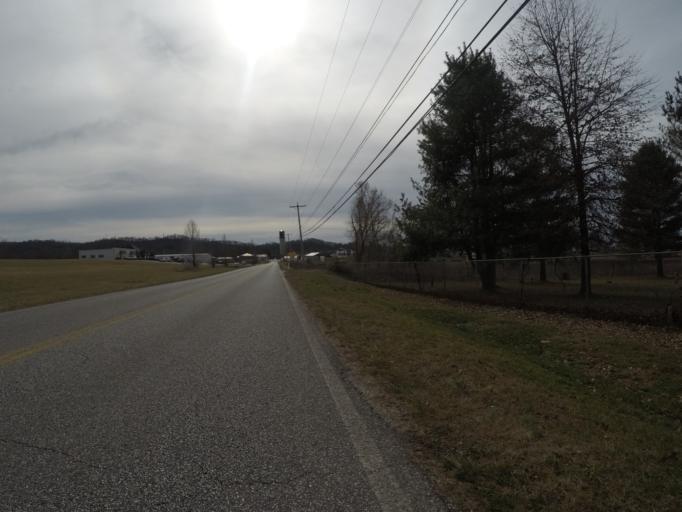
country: US
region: West Virginia
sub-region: Cabell County
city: Pea Ridge
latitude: 38.4419
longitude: -82.3766
